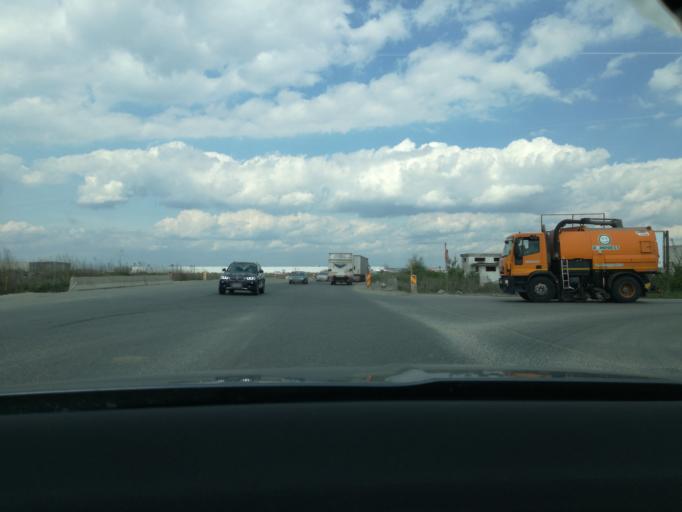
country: RO
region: Ilfov
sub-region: Comuna Chitila
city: Rudeni
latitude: 44.4814
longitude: 25.9719
